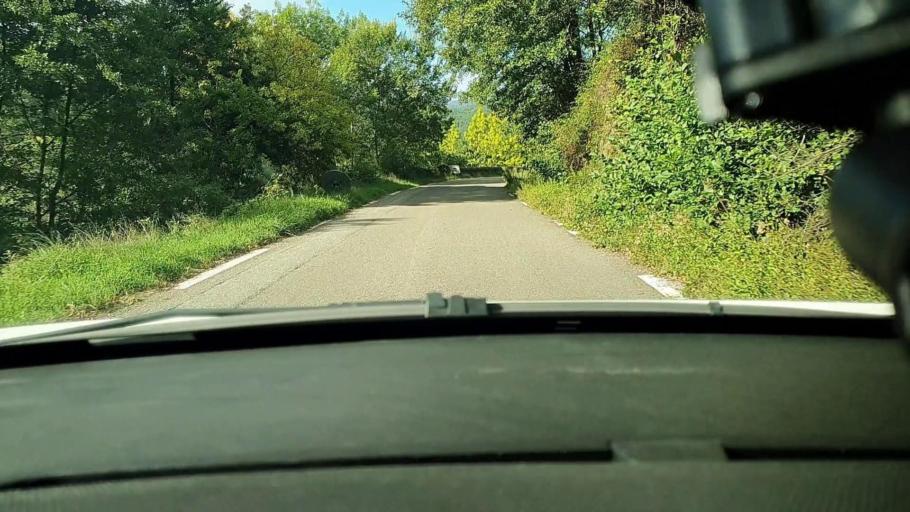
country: FR
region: Languedoc-Roussillon
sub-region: Departement du Gard
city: Besseges
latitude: 44.3594
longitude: 4.0131
